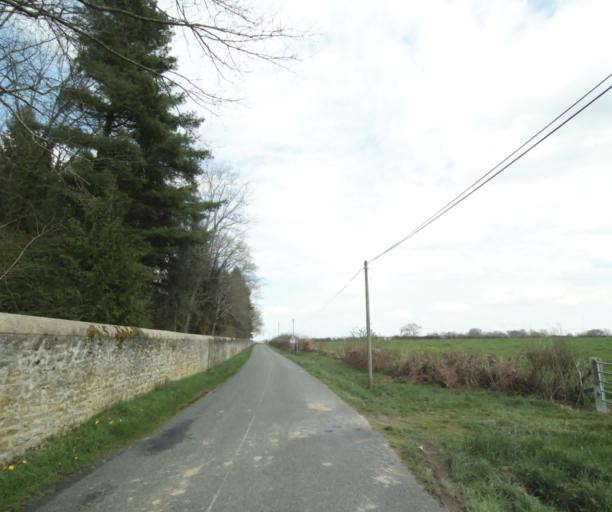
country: FR
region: Bourgogne
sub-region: Departement de Saone-et-Loire
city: Palinges
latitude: 46.5364
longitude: 4.2136
